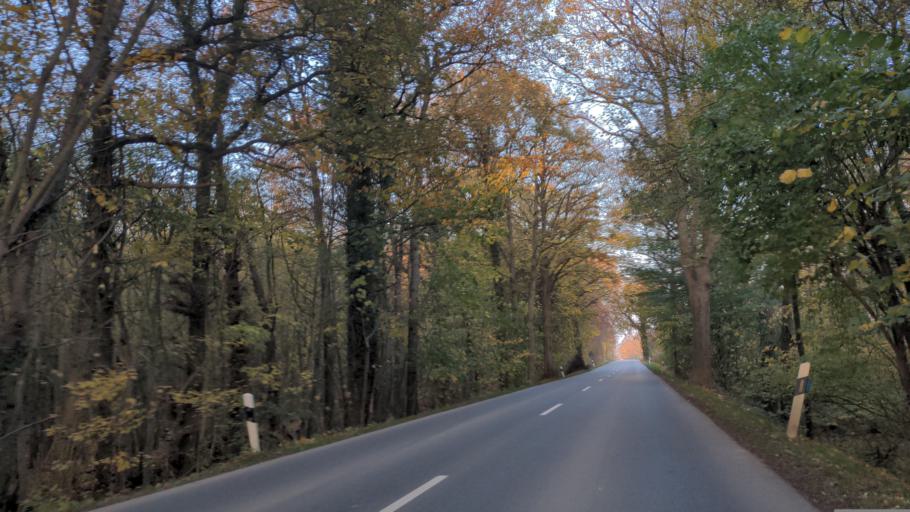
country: DE
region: Schleswig-Holstein
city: Glasau
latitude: 54.1004
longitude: 10.5235
